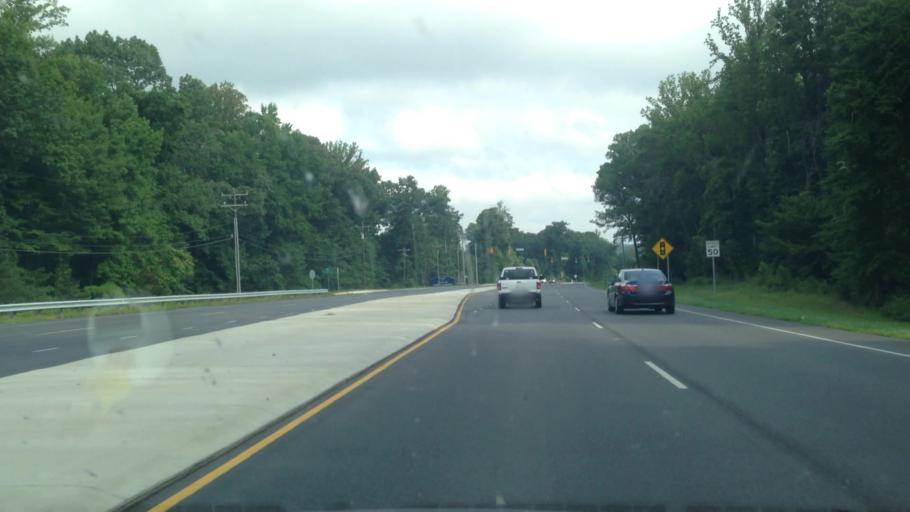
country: US
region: North Carolina
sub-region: Guilford County
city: Summerfield
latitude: 36.1617
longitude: -79.8766
